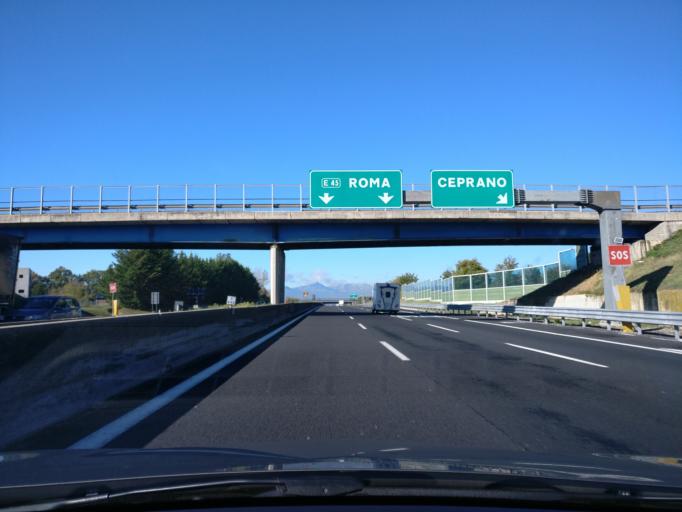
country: IT
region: Latium
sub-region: Provincia di Frosinone
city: Ceprano
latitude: 41.5434
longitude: 13.4957
